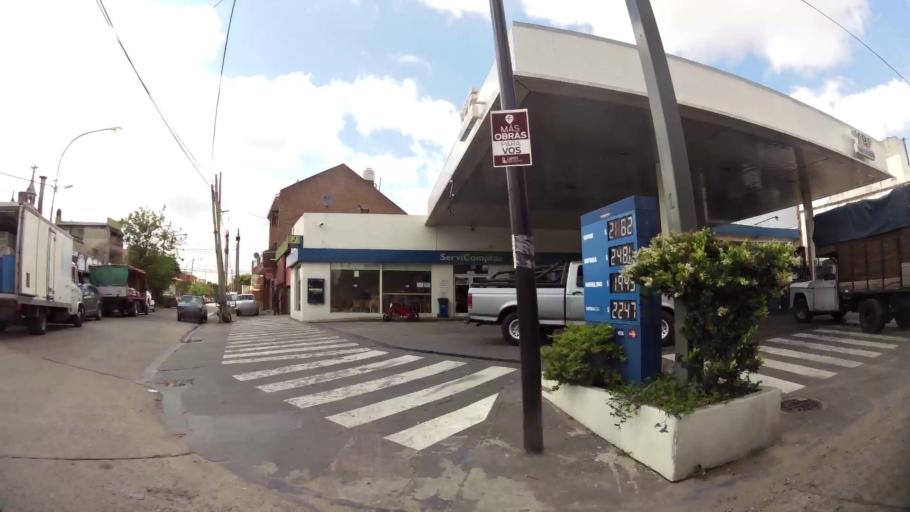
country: AR
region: Buenos Aires
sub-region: Partido de Lanus
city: Lanus
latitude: -34.6894
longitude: -58.4183
